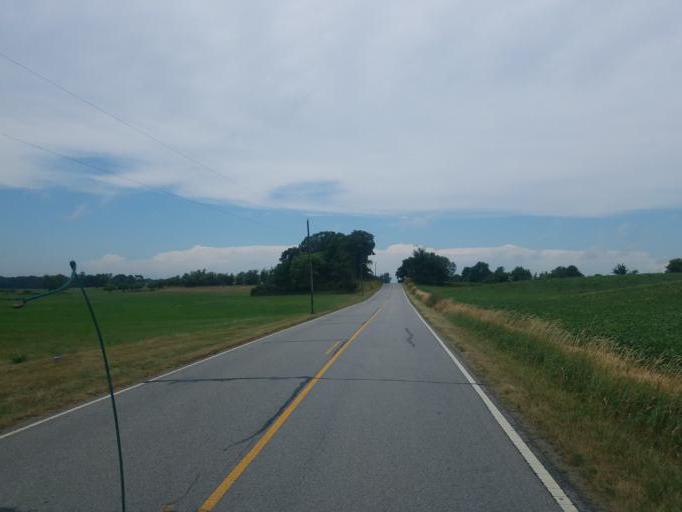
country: US
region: Indiana
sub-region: DeKalb County
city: Butler
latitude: 41.3860
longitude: -84.8629
